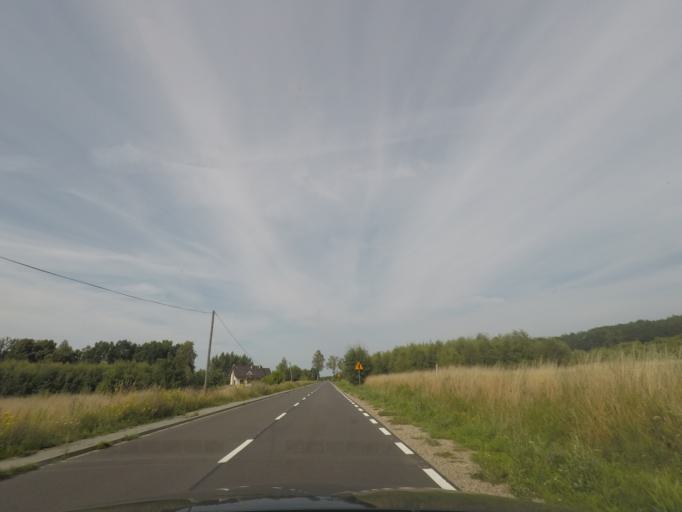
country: PL
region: Pomeranian Voivodeship
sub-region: Powiat slupski
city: Smoldzino
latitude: 54.5979
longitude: 17.1001
